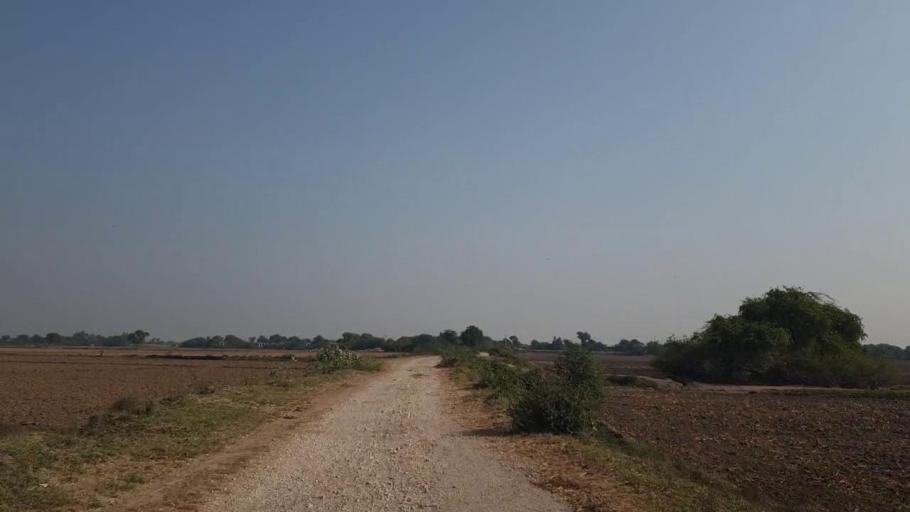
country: PK
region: Sindh
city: Matli
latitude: 25.0055
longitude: 68.6287
